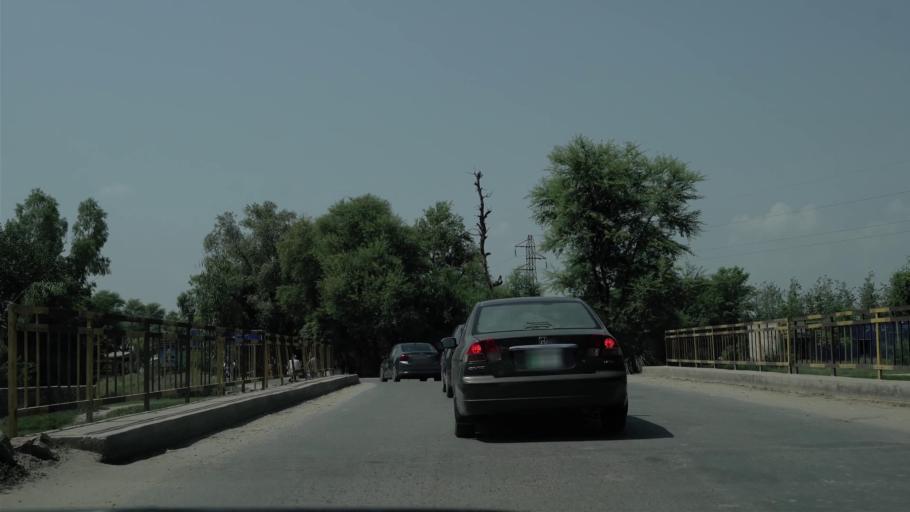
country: PK
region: Punjab
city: Gojra
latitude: 31.1694
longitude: 72.6235
